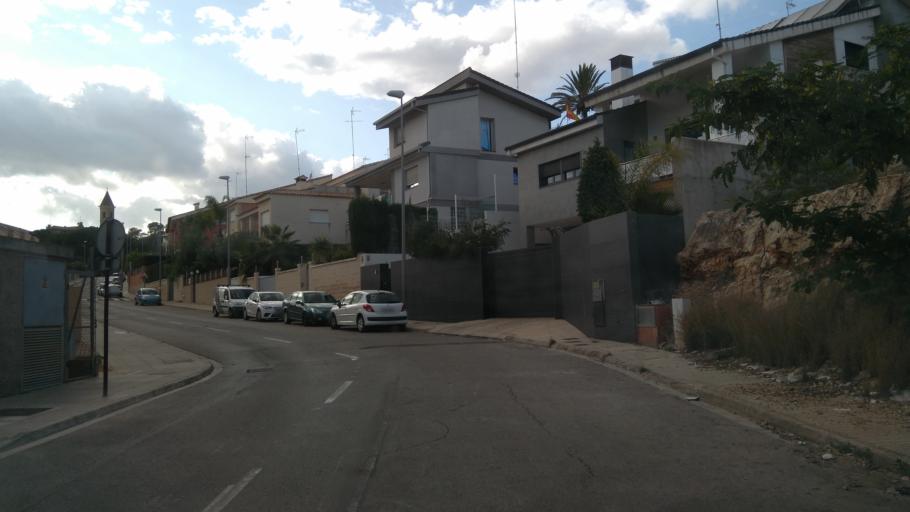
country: ES
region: Valencia
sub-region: Provincia de Valencia
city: Alzira
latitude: 39.1541
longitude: -0.4148
